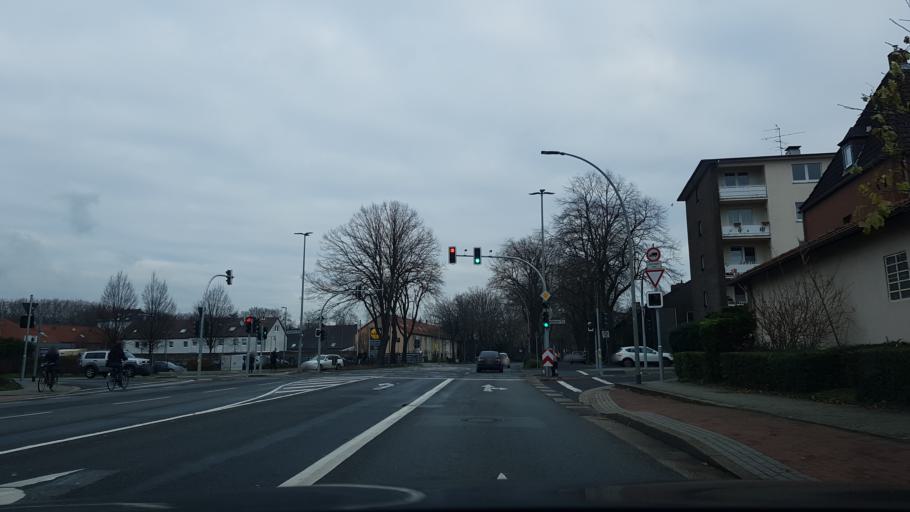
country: DE
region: North Rhine-Westphalia
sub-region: Regierungsbezirk Dusseldorf
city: Hochfeld
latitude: 51.4521
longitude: 6.6985
